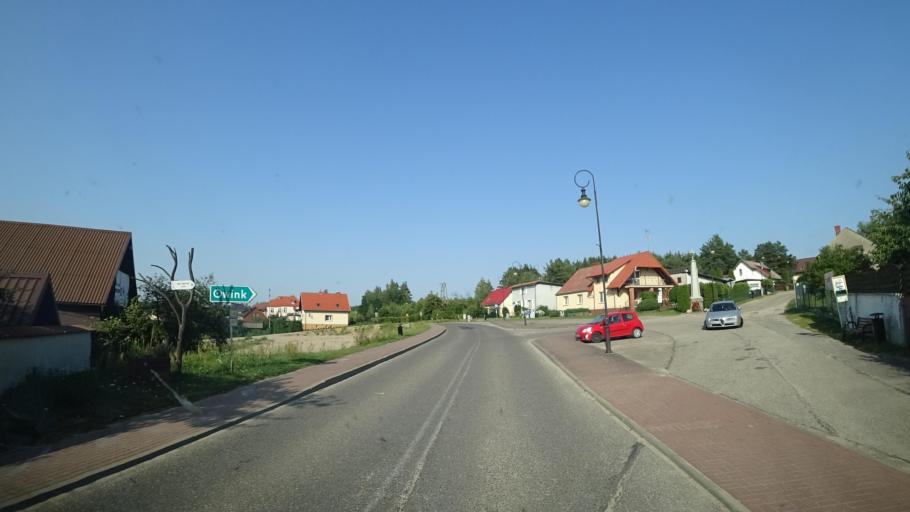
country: PL
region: Pomeranian Voivodeship
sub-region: Powiat bytowski
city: Lipnica
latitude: 53.8609
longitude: 17.5008
